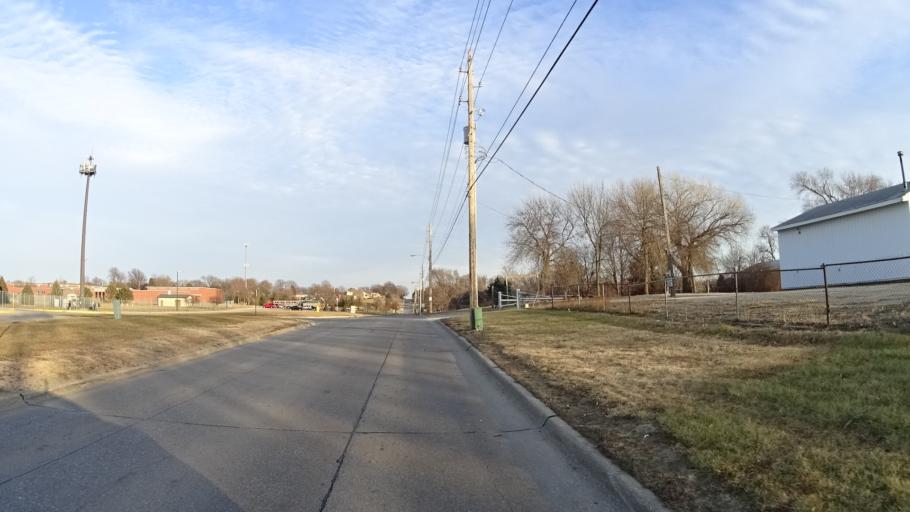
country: US
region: Nebraska
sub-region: Sarpy County
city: La Vista
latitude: 41.1763
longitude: -95.9815
